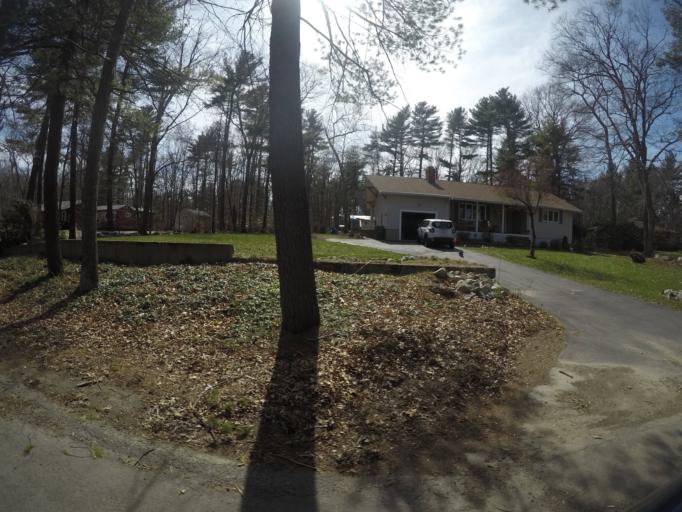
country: US
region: Massachusetts
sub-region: Plymouth County
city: West Bridgewater
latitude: 42.0307
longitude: -71.0676
